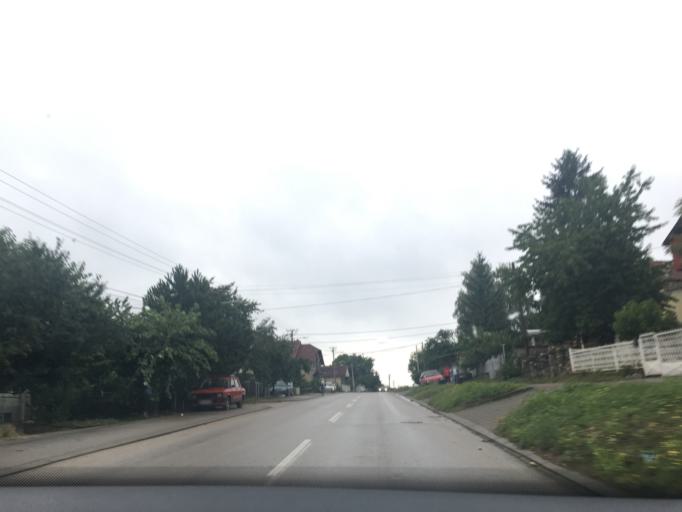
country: RS
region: Central Serbia
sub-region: Nisavski Okrug
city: Aleksinac
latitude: 43.5438
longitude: 21.6988
